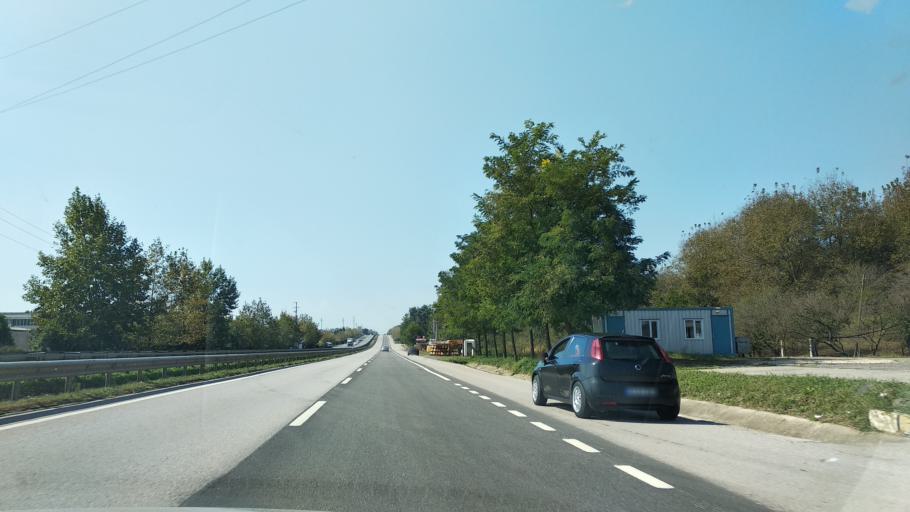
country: TR
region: Kocaeli
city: Derbent
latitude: 40.7321
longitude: 30.1861
